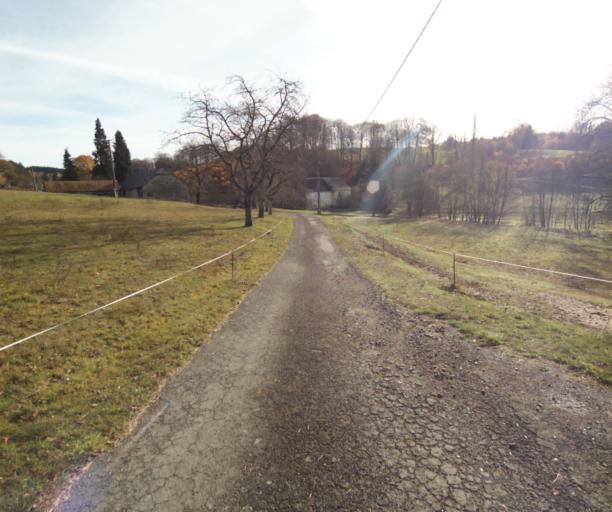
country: FR
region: Limousin
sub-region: Departement de la Correze
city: Cornil
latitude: 45.1943
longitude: 1.7213
